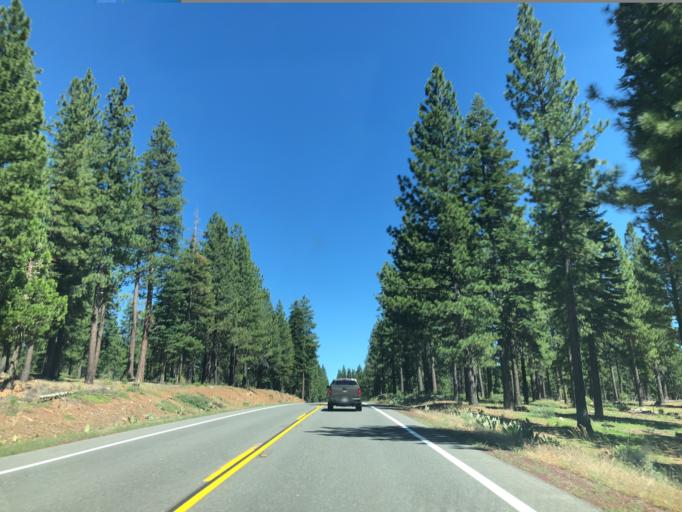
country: US
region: California
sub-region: Lassen County
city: Westwood
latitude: 40.4406
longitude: -120.8583
